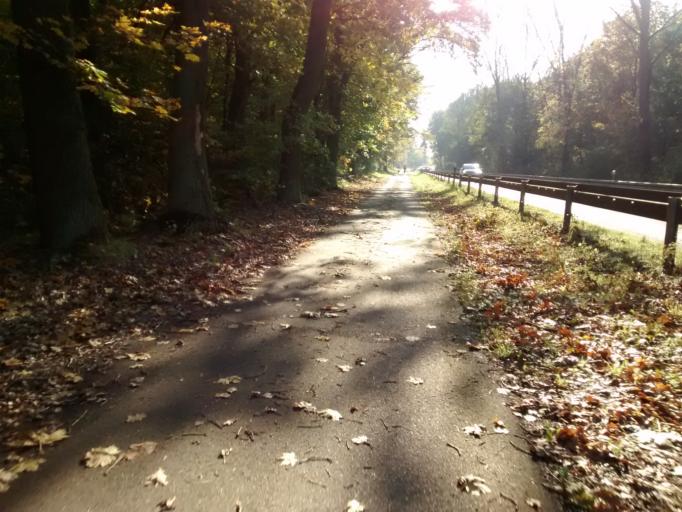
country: DE
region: Brandenburg
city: Hennigsdorf
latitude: 52.6395
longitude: 13.2222
